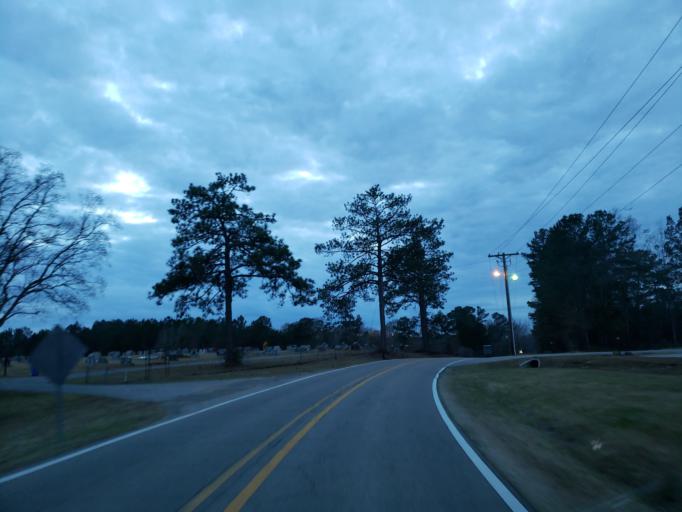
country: US
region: Mississippi
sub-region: Forrest County
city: Petal
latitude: 31.3433
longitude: -89.2464
